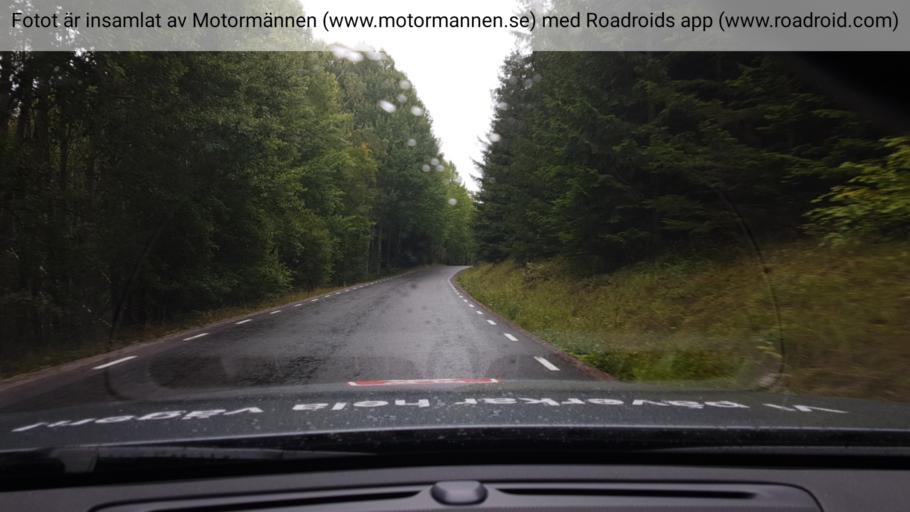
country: SE
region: Stockholm
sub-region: Nynashamns Kommun
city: Osmo
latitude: 59.0388
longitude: 17.9270
